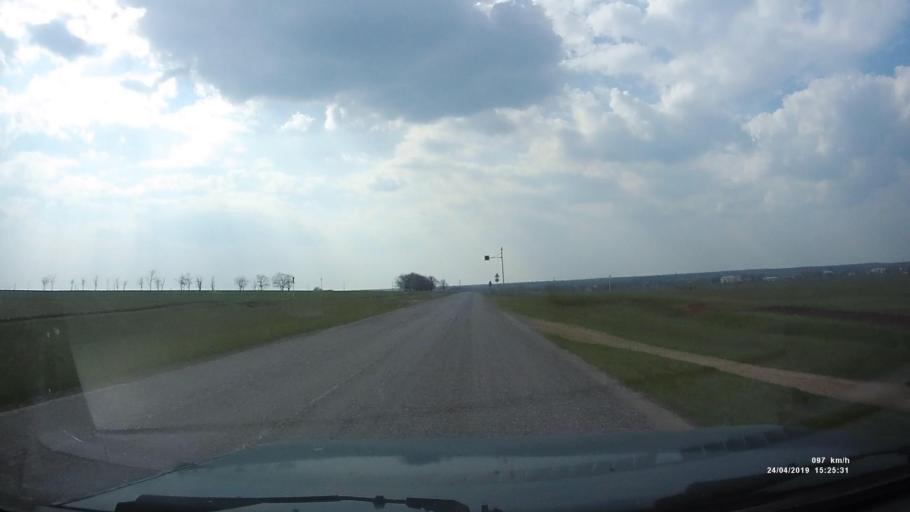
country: RU
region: Rostov
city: Remontnoye
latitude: 46.5528
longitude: 43.0464
